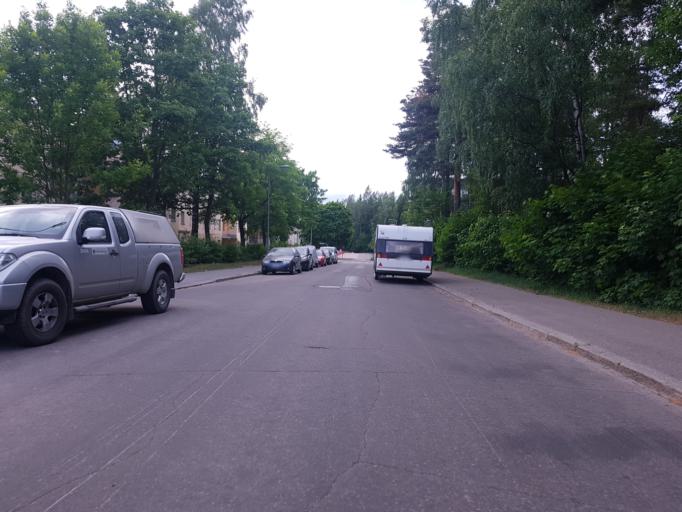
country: FI
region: Uusimaa
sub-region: Helsinki
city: Helsinki
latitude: 60.2341
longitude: 24.9572
